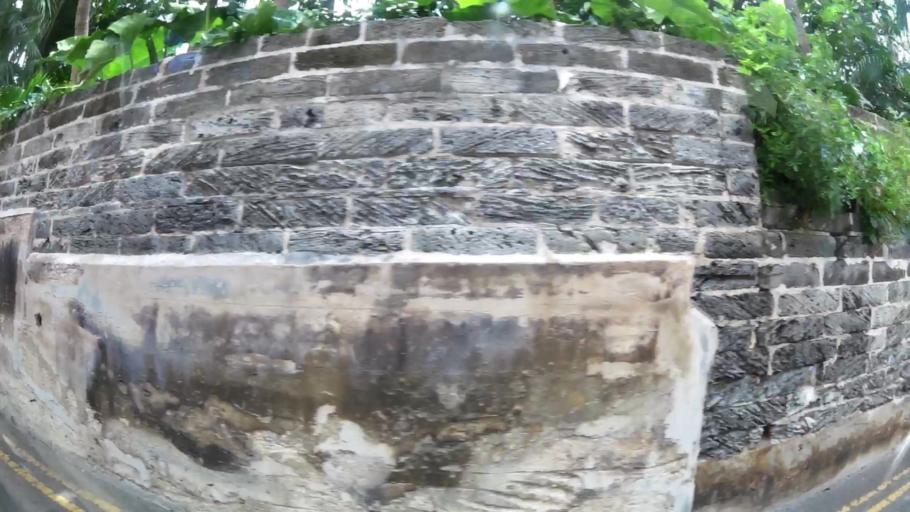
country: BM
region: Hamilton city
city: Hamilton
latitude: 32.2924
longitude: -64.7873
